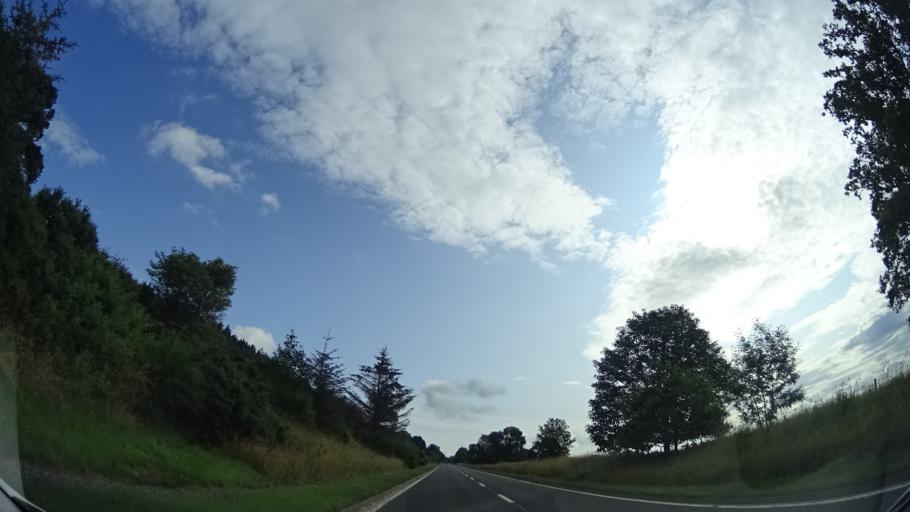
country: GB
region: Scotland
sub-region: Highland
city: Muir of Ord
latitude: 57.5597
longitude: -4.4979
